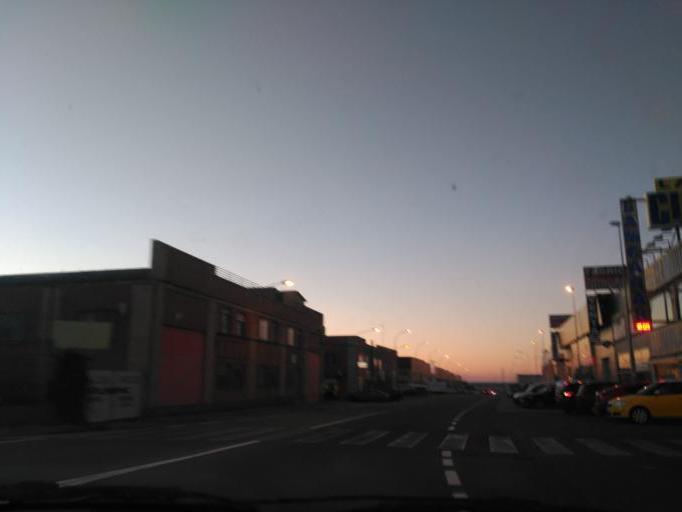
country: ES
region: Castille and Leon
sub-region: Provincia de Salamanca
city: Villares de la Reina
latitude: 40.9937
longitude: -5.6468
